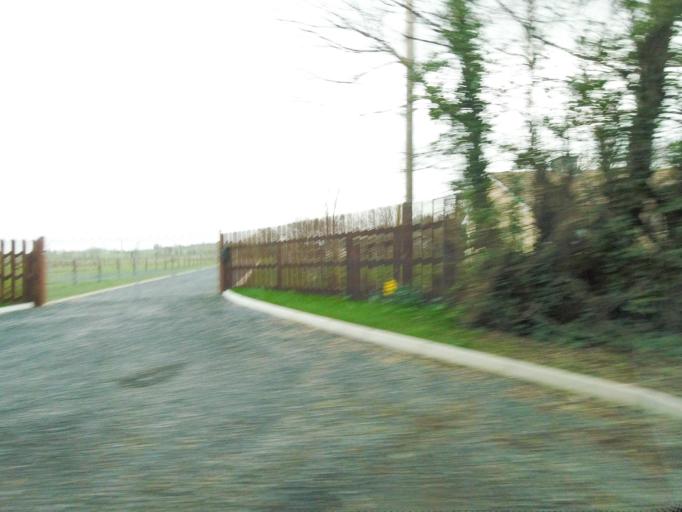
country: IE
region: Leinster
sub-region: Kildare
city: Naas
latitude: 53.1743
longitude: -6.6828
